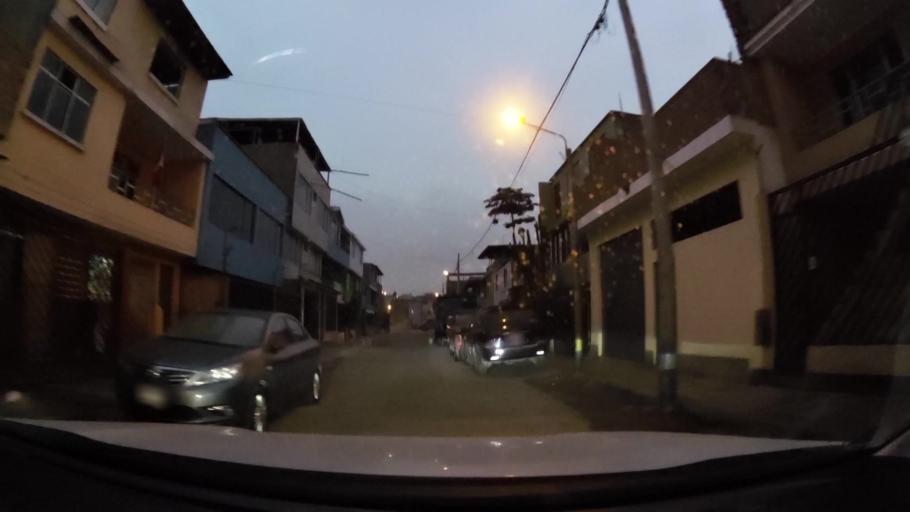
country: PE
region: Lima
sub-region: Lima
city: Surco
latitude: -12.1442
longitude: -76.9756
